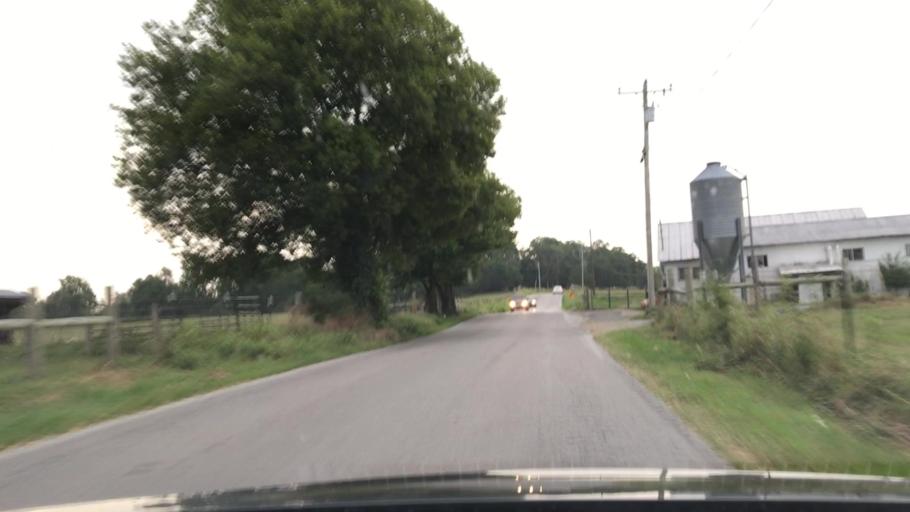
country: US
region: Tennessee
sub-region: Williamson County
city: Nolensville
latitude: 35.9773
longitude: -86.6770
